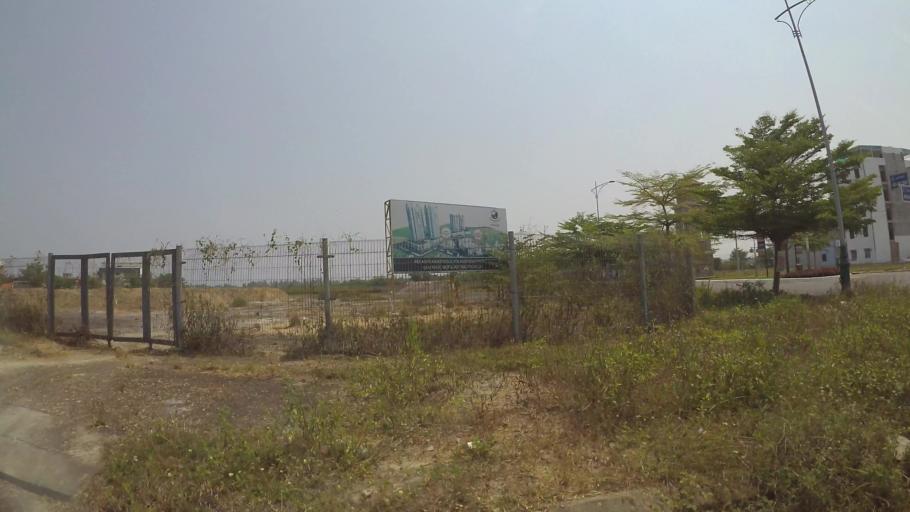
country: VN
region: Da Nang
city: Ngu Hanh Son
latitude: 15.9886
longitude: 108.2582
